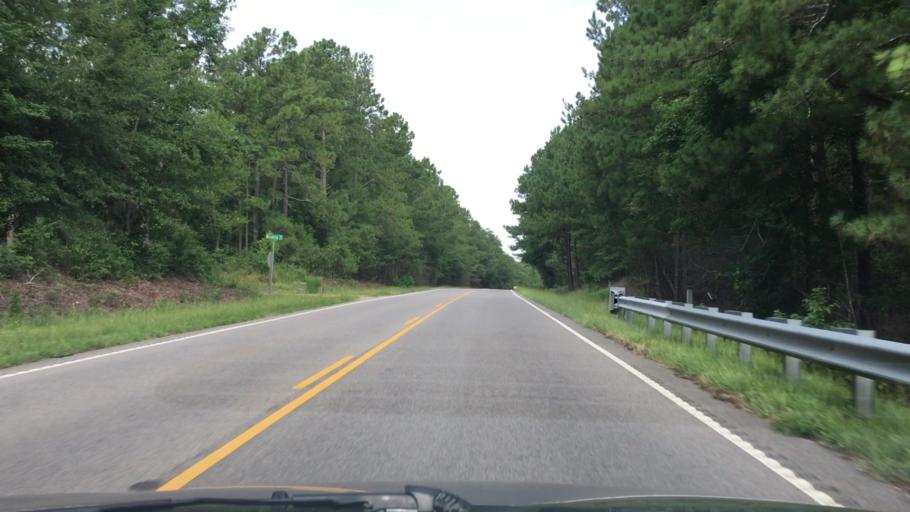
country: US
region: South Carolina
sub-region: Lexington County
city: Leesville
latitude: 33.6763
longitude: -81.4325
